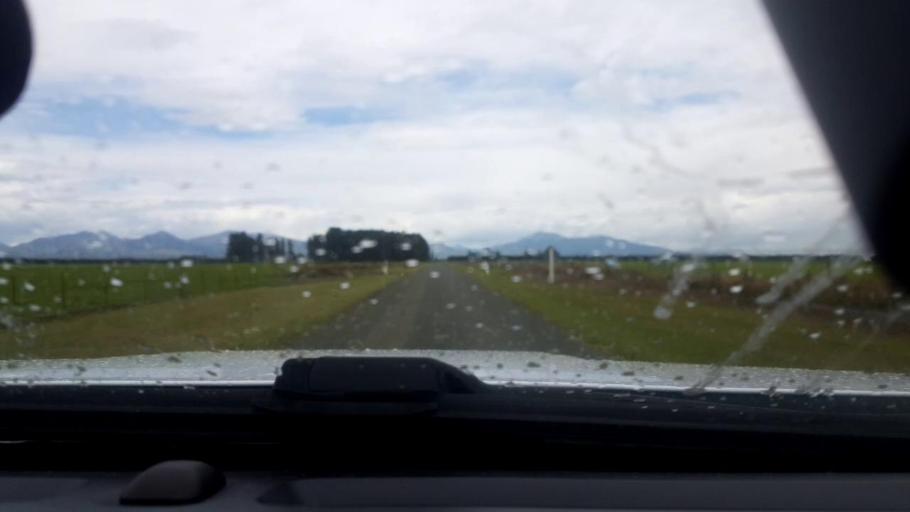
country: NZ
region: Canterbury
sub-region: Timaru District
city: Pleasant Point
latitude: -44.1130
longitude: 171.3535
